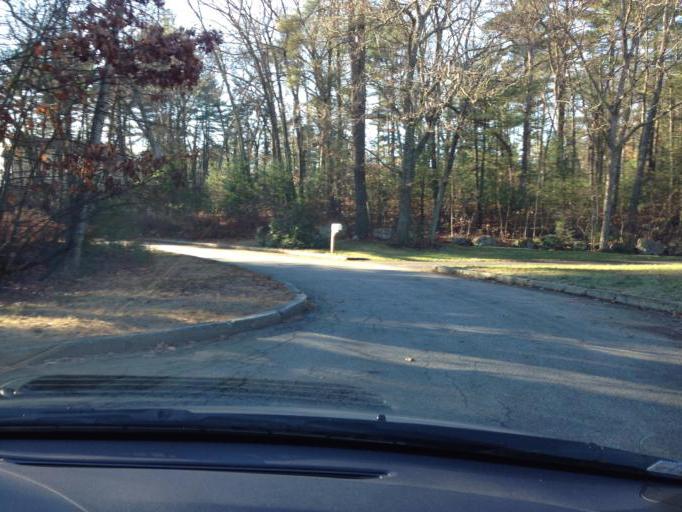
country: US
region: Massachusetts
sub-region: Middlesex County
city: Bedford
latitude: 42.5160
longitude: -71.2764
